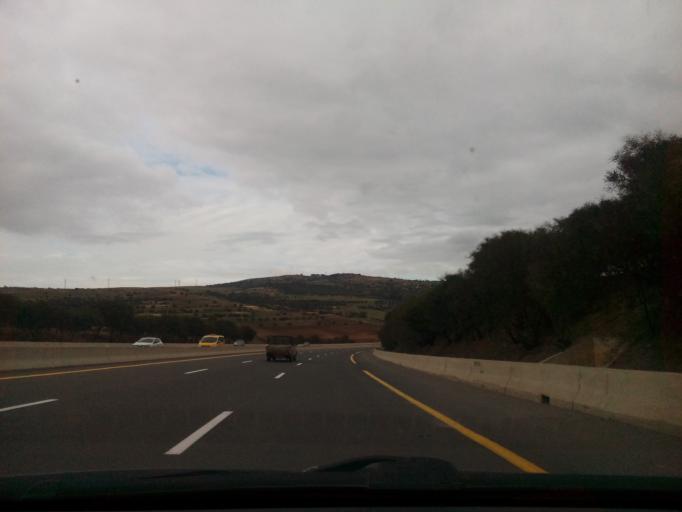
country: DZ
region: Sidi Bel Abbes
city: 'Ain el Berd
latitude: 35.4015
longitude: -0.4921
